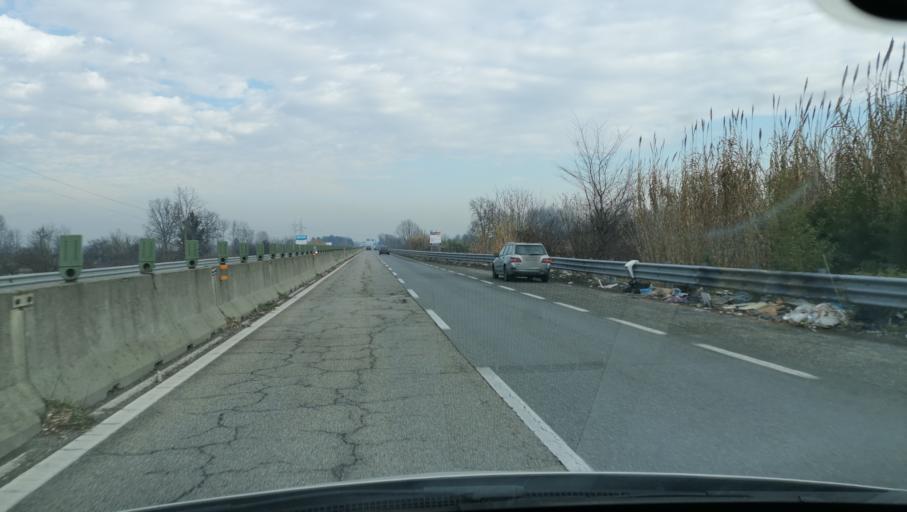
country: IT
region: Piedmont
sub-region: Provincia di Torino
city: Castiglione Torinese
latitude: 45.1406
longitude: 7.7940
